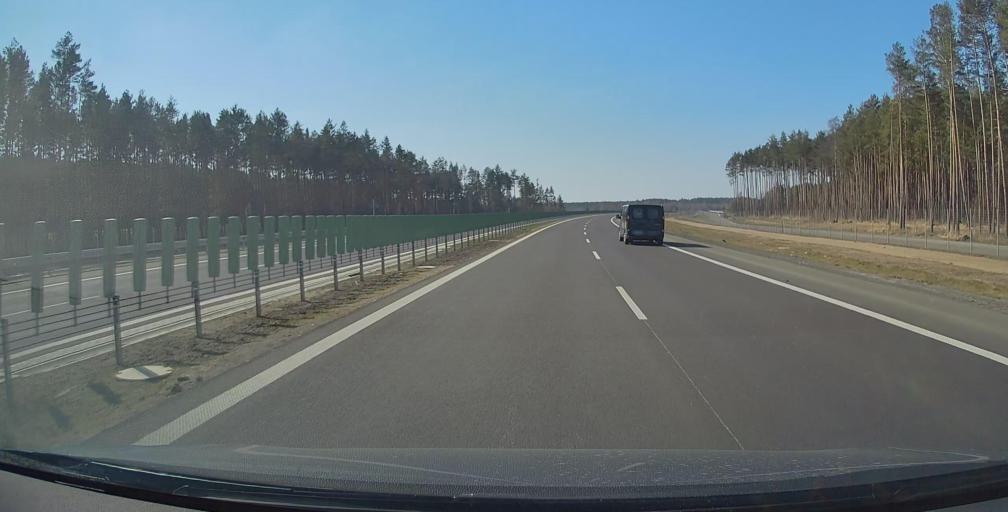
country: PL
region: Subcarpathian Voivodeship
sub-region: Powiat nizanski
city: Przedzel
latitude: 50.4789
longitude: 22.1838
